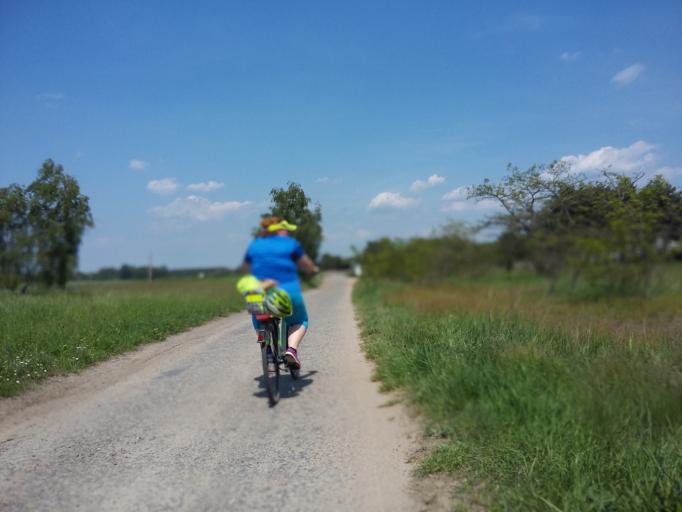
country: AT
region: Lower Austria
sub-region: Politischer Bezirk Ganserndorf
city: Drosing
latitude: 48.5099
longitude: 16.9580
